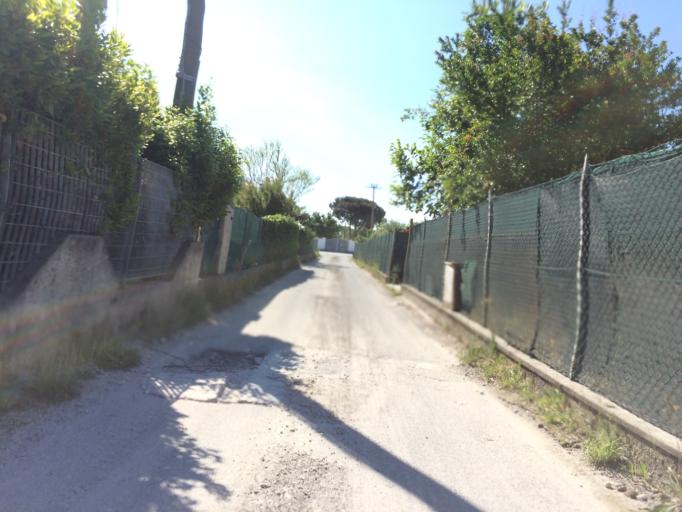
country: IT
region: Tuscany
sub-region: Provincia di Massa-Carrara
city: Carrara
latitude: 44.0307
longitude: 10.0826
